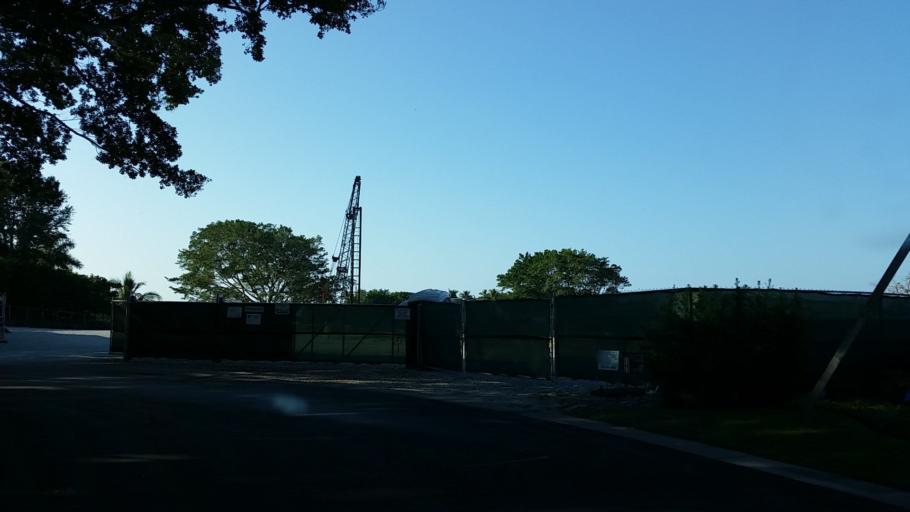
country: US
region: Florida
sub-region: Collier County
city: Naples
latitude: 26.1004
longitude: -81.7961
